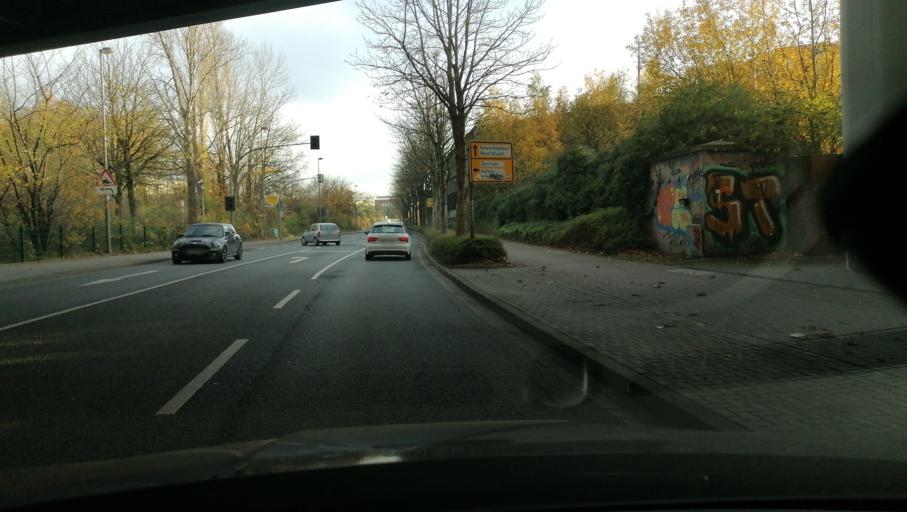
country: DE
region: North Rhine-Westphalia
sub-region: Regierungsbezirk Arnsberg
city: Dortmund
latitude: 51.5241
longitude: 7.4340
